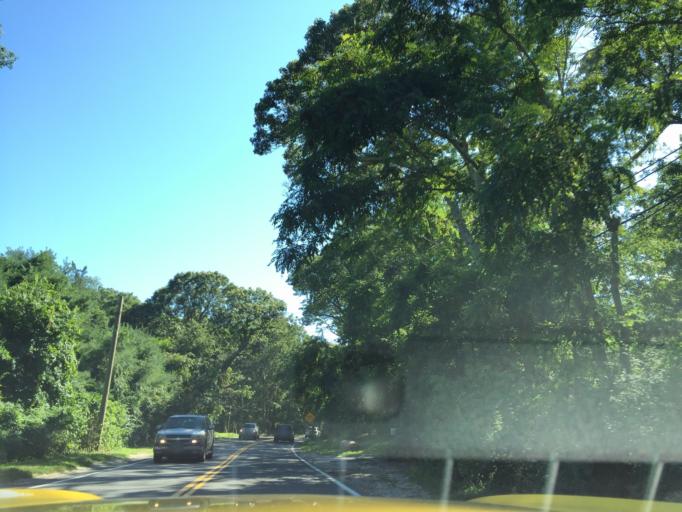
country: US
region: New York
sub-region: Suffolk County
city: North Sea
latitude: 40.9469
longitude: -72.3979
